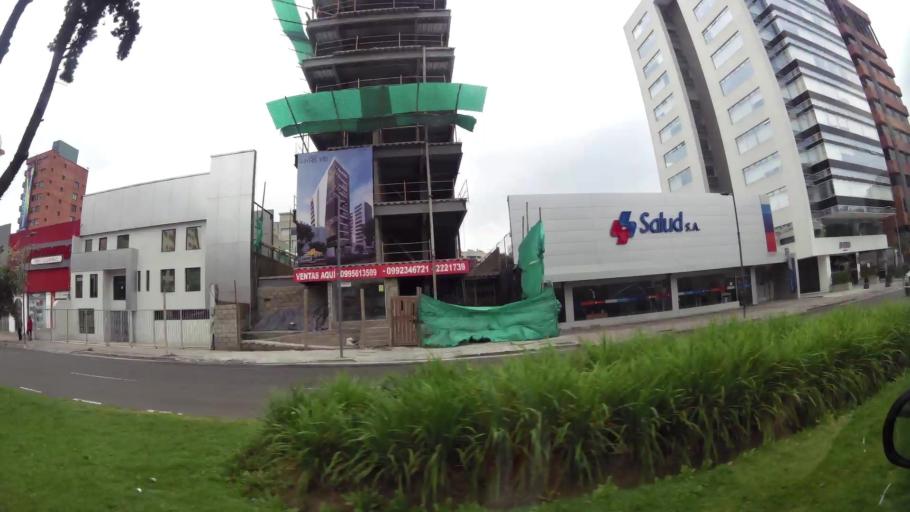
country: EC
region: Pichincha
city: Quito
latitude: -0.1897
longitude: -78.4821
